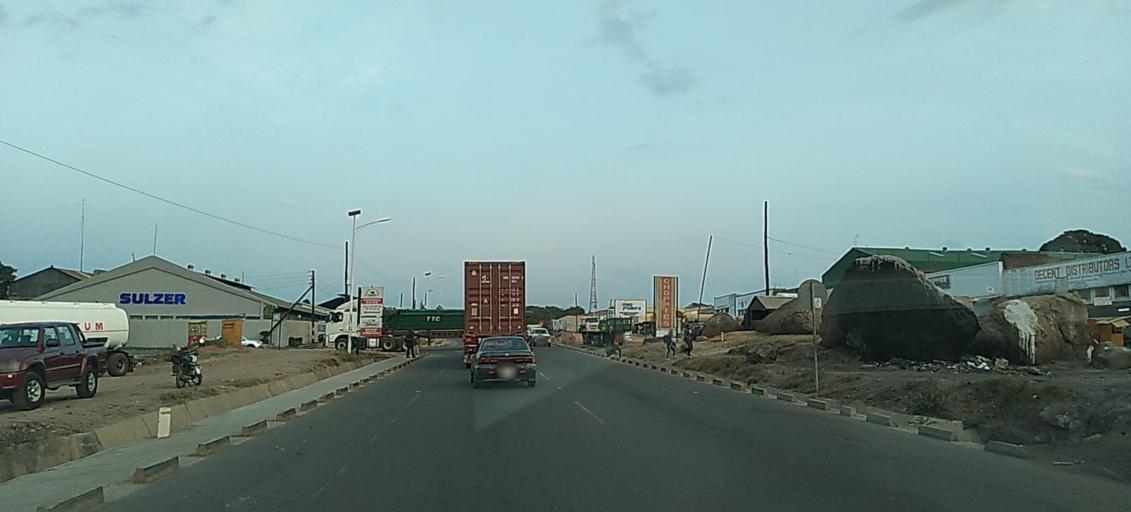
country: ZM
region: Copperbelt
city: Chingola
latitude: -12.5455
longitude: 27.8515
